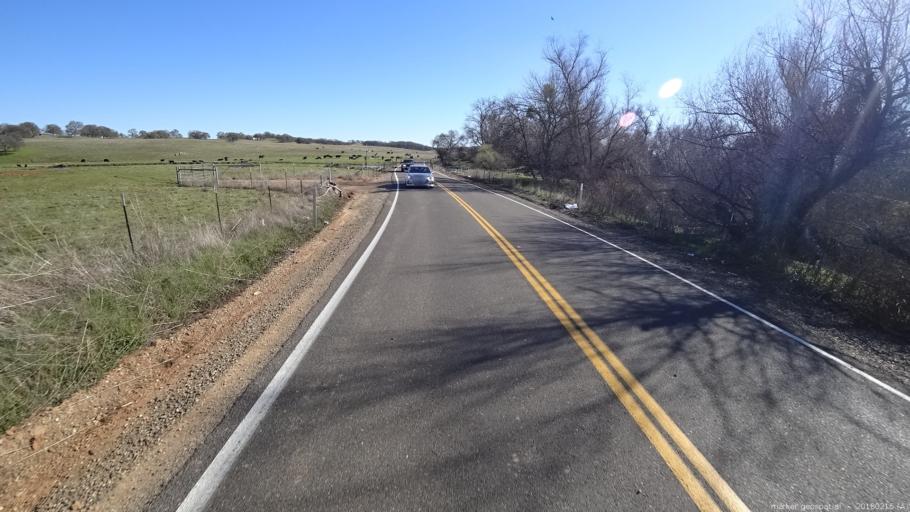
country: US
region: California
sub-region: Sacramento County
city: Rancho Murieta
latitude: 38.5500
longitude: -121.1137
